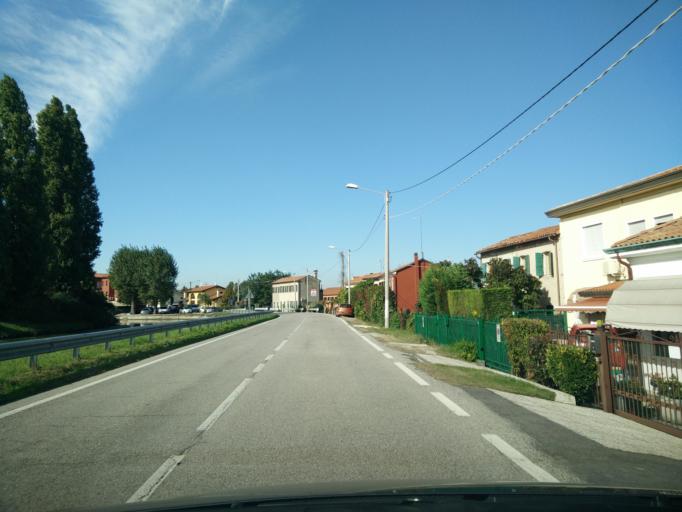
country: IT
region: Veneto
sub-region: Provincia di Venezia
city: Mestre
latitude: 45.4347
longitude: 12.2118
